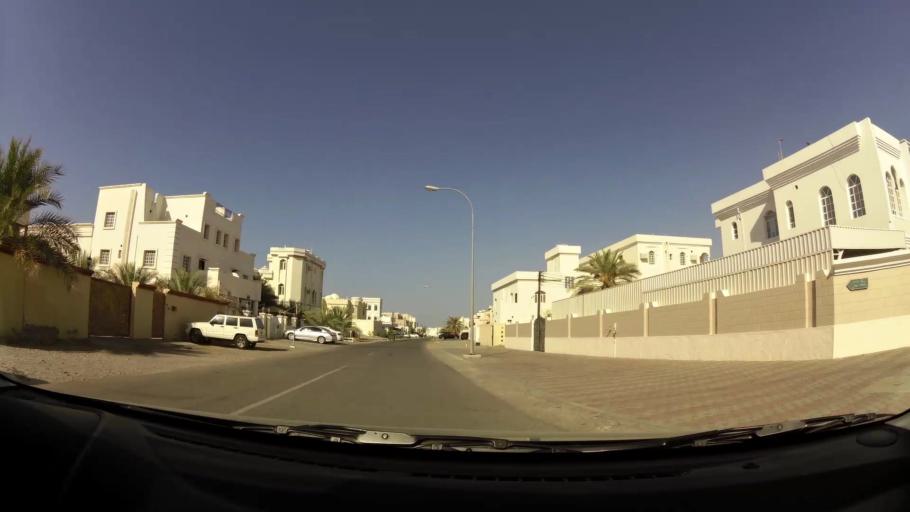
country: OM
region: Muhafazat Masqat
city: As Sib al Jadidah
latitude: 23.6215
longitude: 58.2064
